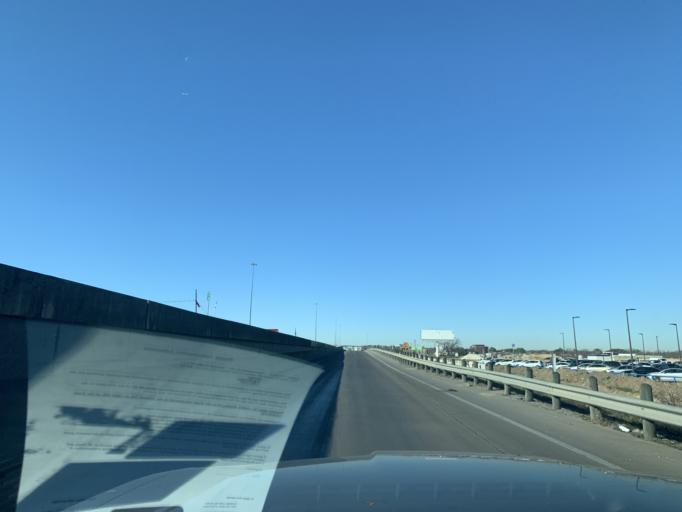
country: US
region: Texas
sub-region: Dallas County
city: Grand Prairie
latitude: 32.7592
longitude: -96.9968
